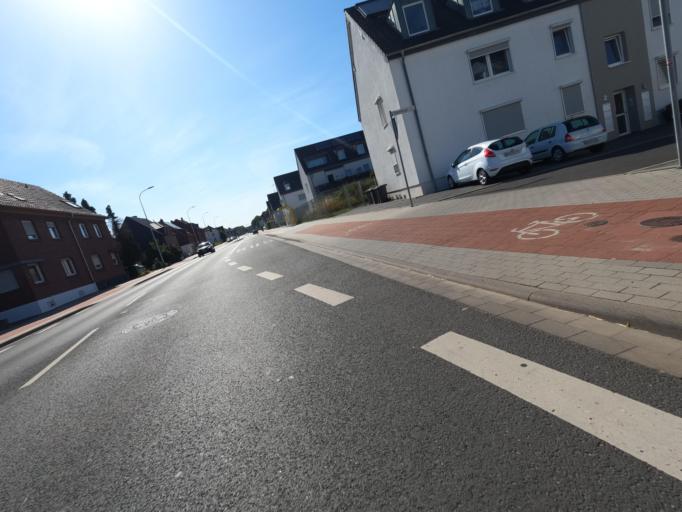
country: DE
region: North Rhine-Westphalia
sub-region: Regierungsbezirk Koln
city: Heinsberg
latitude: 51.0590
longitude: 6.1228
